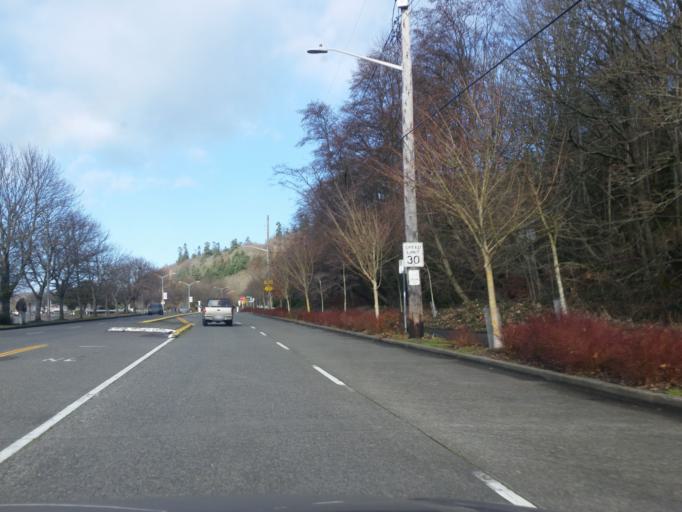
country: US
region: Washington
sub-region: King County
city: Shoreline
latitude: 47.6865
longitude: -122.4028
